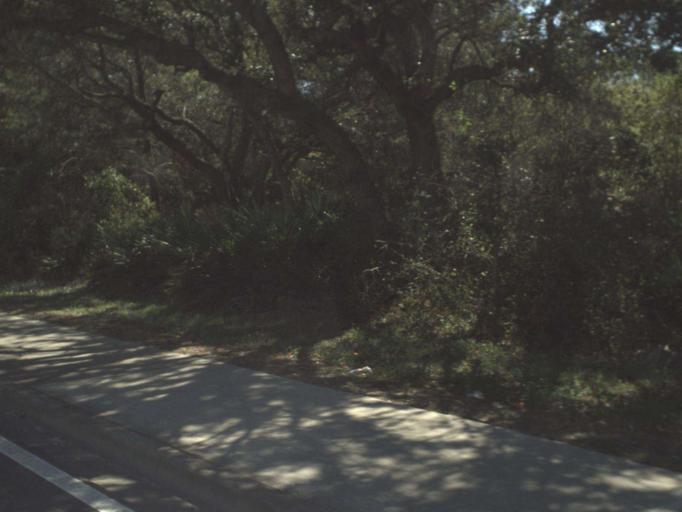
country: US
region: Florida
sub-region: Walton County
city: Miramar Beach
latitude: 30.3790
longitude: -86.3215
